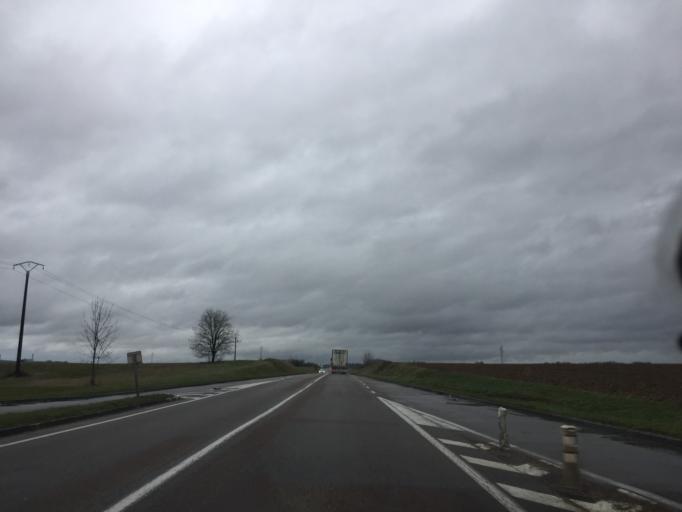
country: FR
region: Franche-Comte
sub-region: Departement du Jura
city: Dole
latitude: 47.1163
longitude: 5.5385
